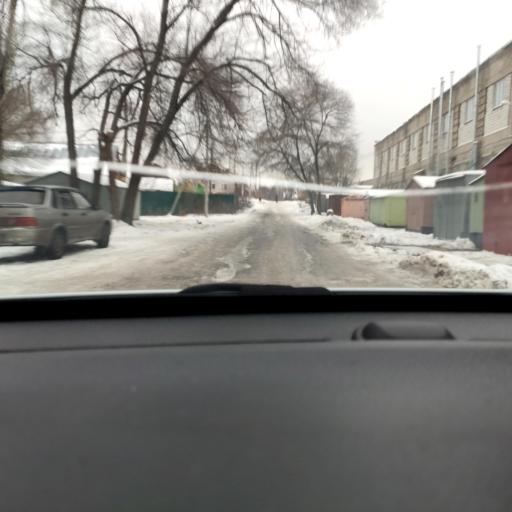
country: RU
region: Voronezj
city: Somovo
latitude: 51.7436
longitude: 39.3586
